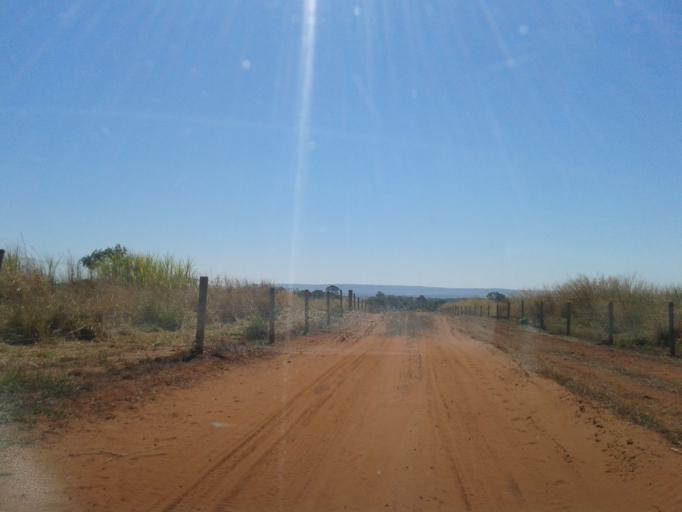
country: BR
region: Minas Gerais
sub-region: Santa Vitoria
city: Santa Vitoria
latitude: -19.1438
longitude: -50.2024
